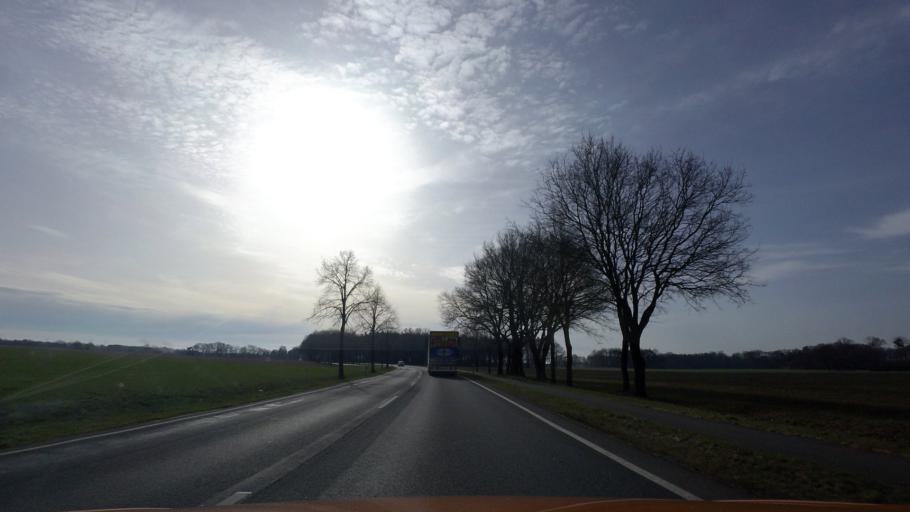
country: DE
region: Lower Saxony
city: Scholen
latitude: 52.7213
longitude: 8.7633
